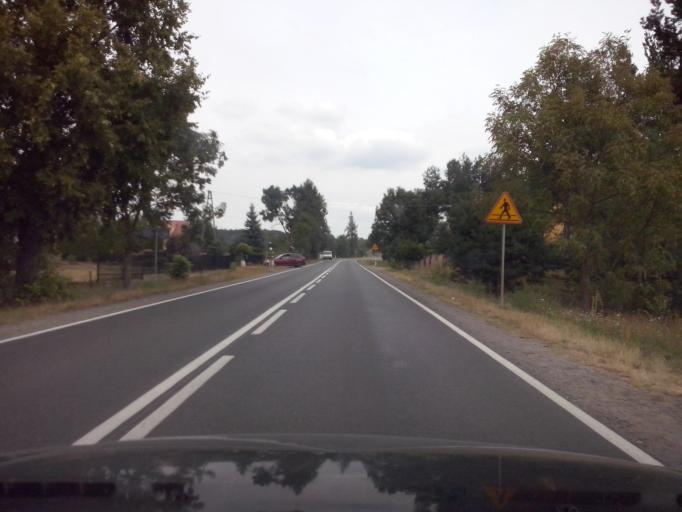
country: PL
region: Swietokrzyskie
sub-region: Powiat kielecki
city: Rakow
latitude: 50.6780
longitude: 21.0487
